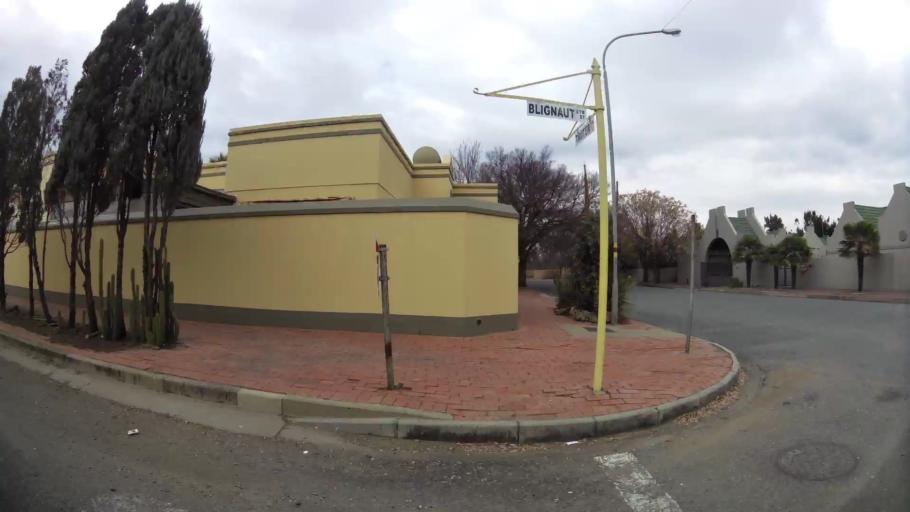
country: ZA
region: Orange Free State
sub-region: Fezile Dabi District Municipality
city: Kroonstad
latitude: -27.6715
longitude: 27.2340
